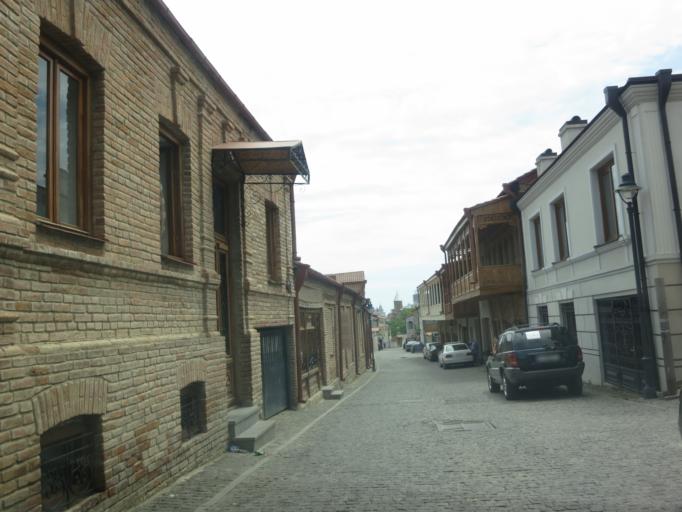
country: GE
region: Kakheti
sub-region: Telavi
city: Telavi
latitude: 41.9209
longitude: 45.4638
